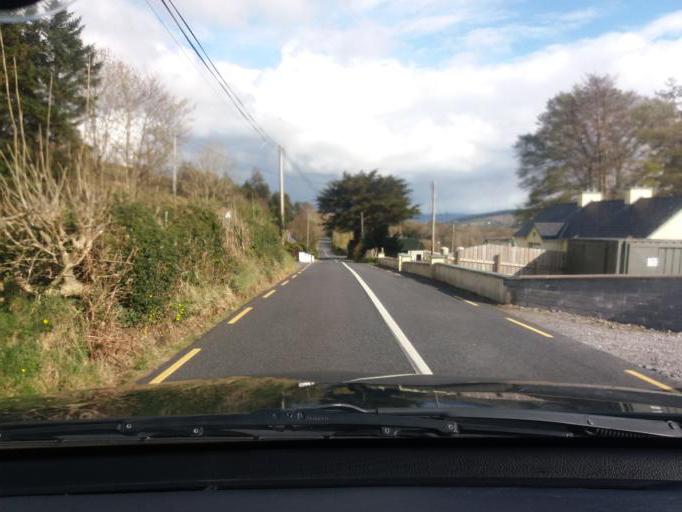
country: IE
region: Connaught
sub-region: County Leitrim
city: Kinlough
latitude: 54.3714
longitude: -8.2721
